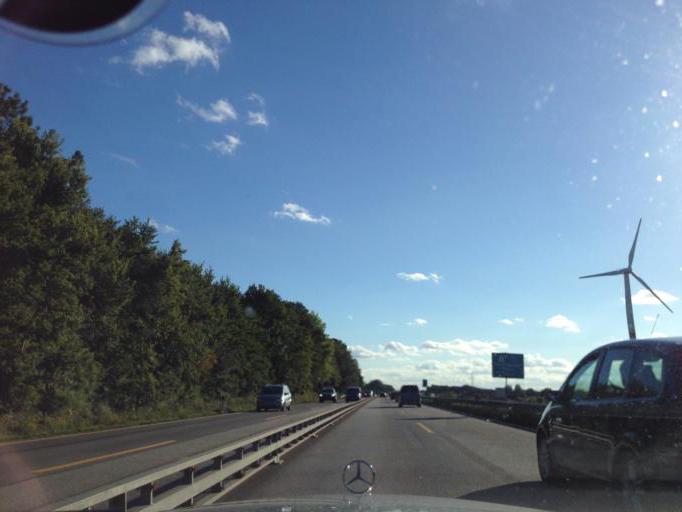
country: DE
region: Schleswig-Holstein
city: Loop
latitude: 54.1307
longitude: 9.9584
